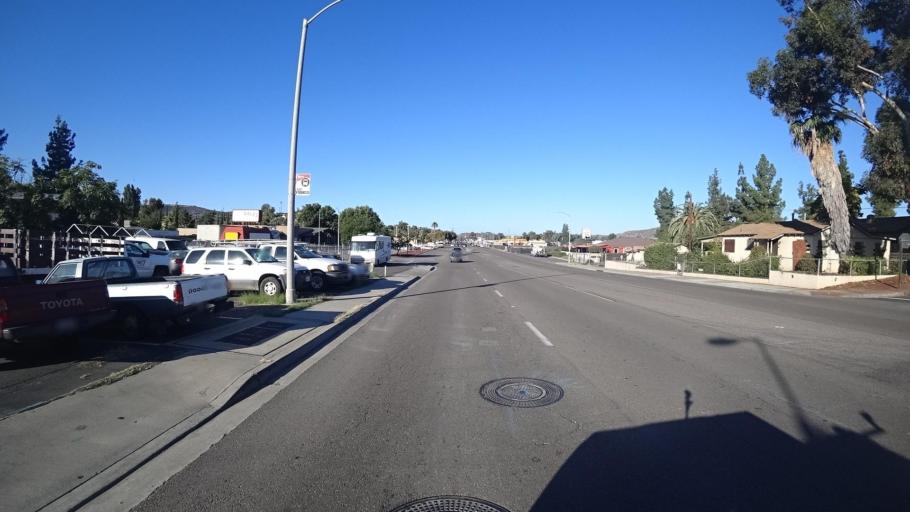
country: US
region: California
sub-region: San Diego County
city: Lakeside
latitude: 32.8572
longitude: -116.9225
